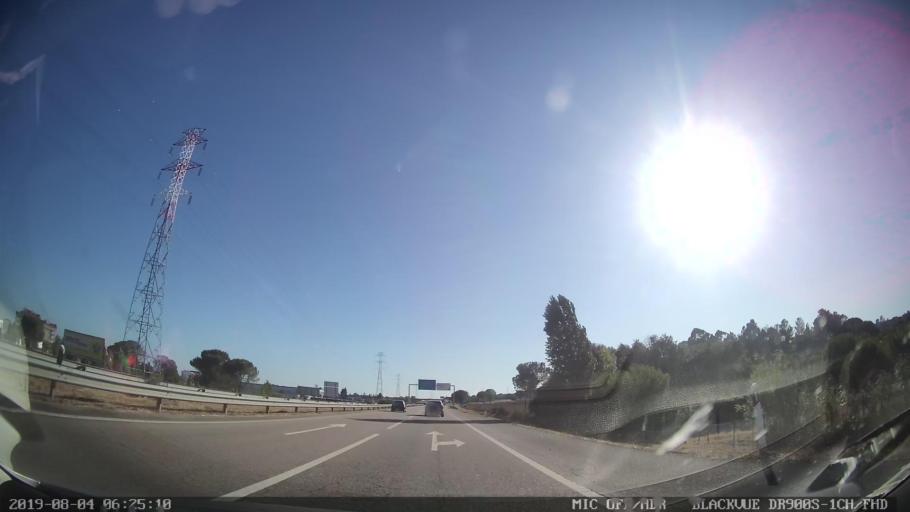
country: PT
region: Santarem
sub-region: Entroncamento
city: Entroncamento
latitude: 39.4777
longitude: -8.4830
